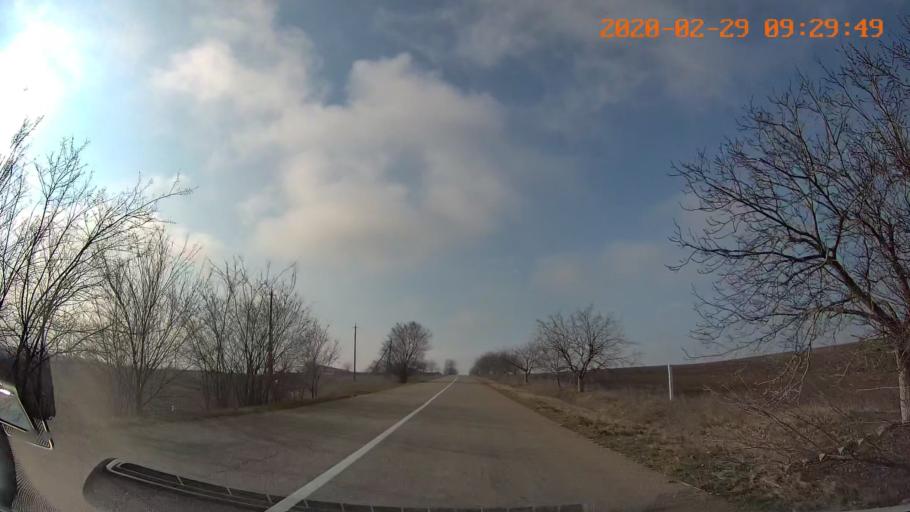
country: UA
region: Odessa
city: Lymanske
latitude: 46.6738
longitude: 29.9193
